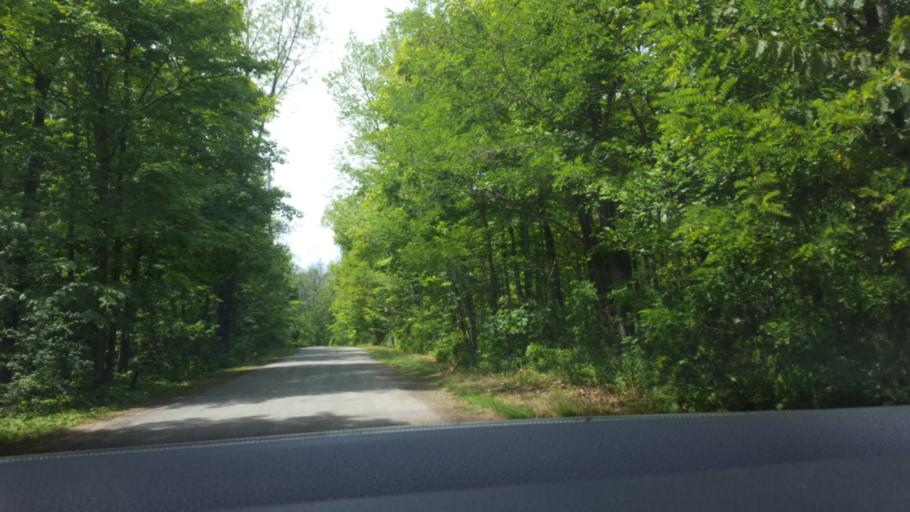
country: CA
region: Ontario
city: Hamilton
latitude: 43.1895
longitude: -79.5737
